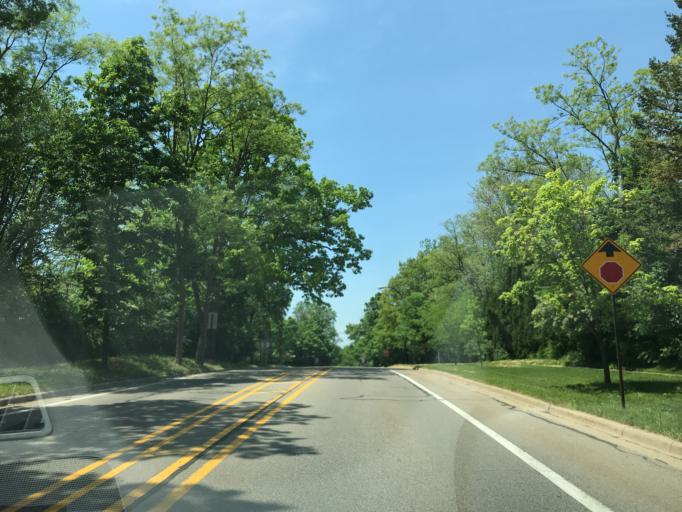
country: US
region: Michigan
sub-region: Washtenaw County
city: Ann Arbor
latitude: 42.2881
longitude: -83.6909
